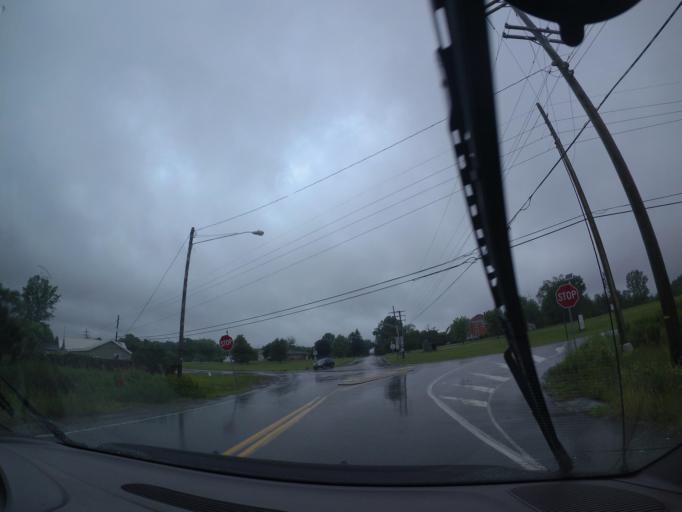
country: US
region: Pennsylvania
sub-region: Erie County
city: Fairview
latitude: 41.9972
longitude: -80.2342
